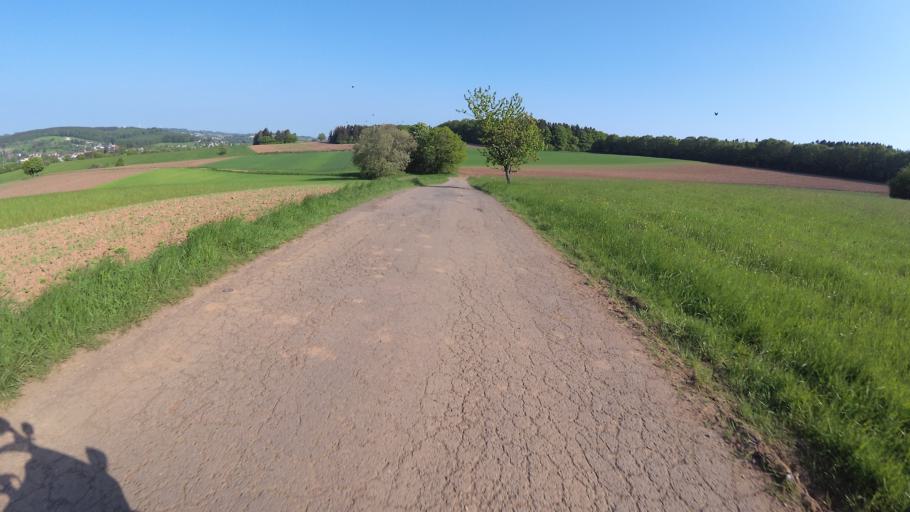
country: DE
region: Saarland
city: Illingen
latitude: 49.3967
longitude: 7.0157
